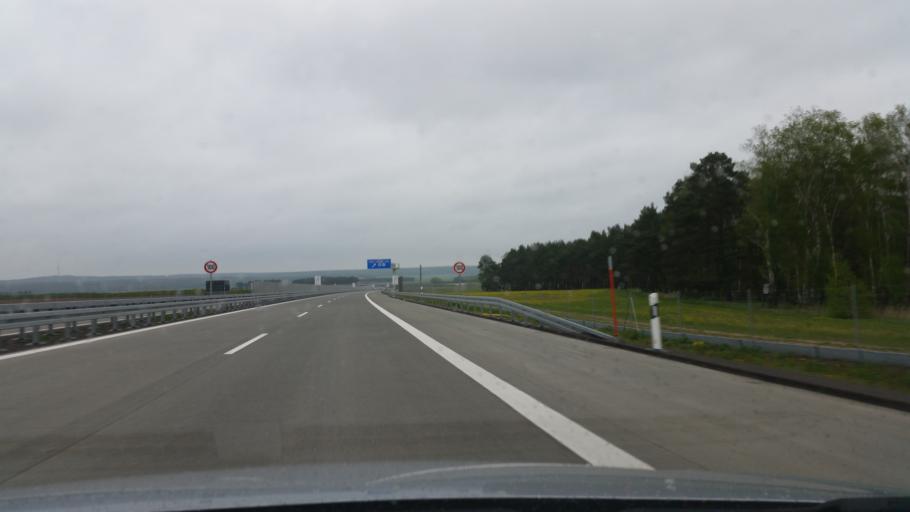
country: DE
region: Saxony-Anhalt
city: Burgstall
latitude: 52.3939
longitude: 11.6293
